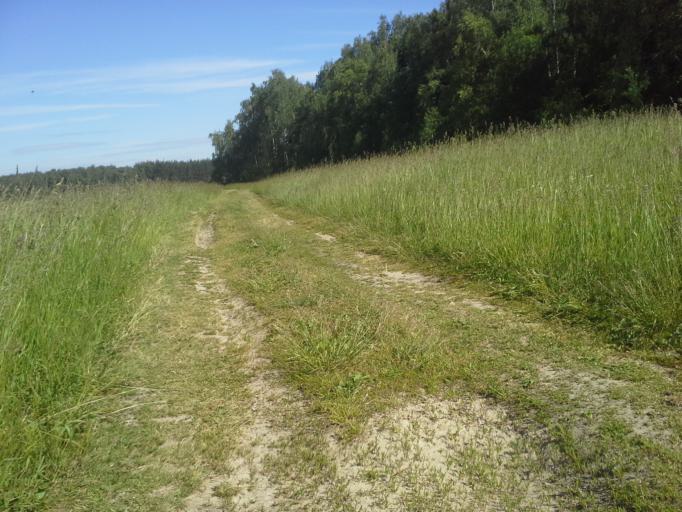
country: RU
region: Moskovskaya
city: Dubrovitsy
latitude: 55.4682
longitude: 37.4352
